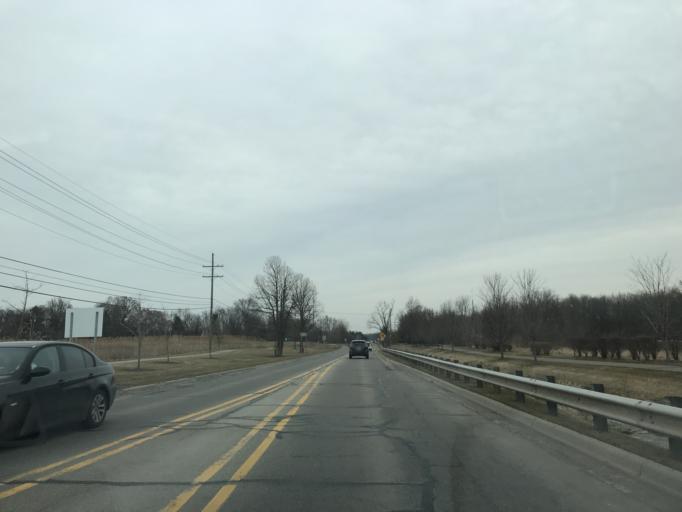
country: US
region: Michigan
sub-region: Oakland County
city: Wixom
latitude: 42.4818
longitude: -83.5349
